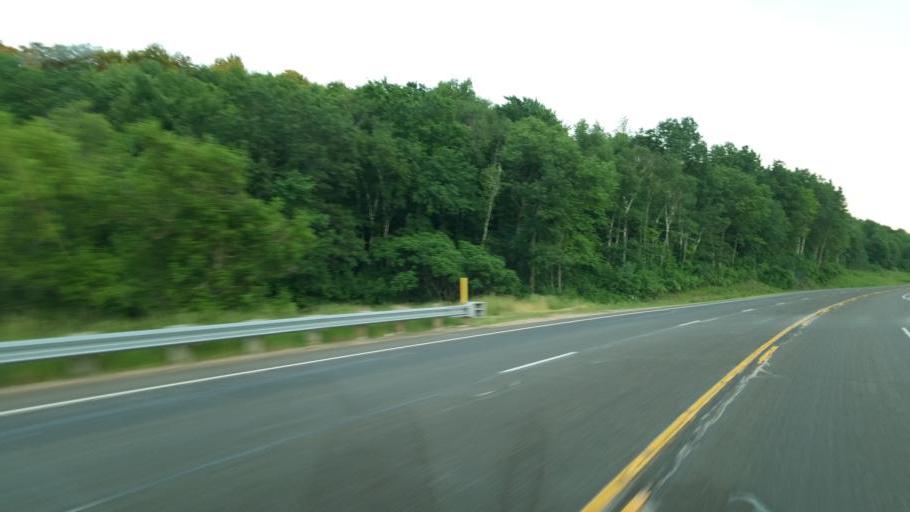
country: US
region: Wisconsin
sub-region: Monroe County
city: Tomah
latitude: 43.8856
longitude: -90.4807
